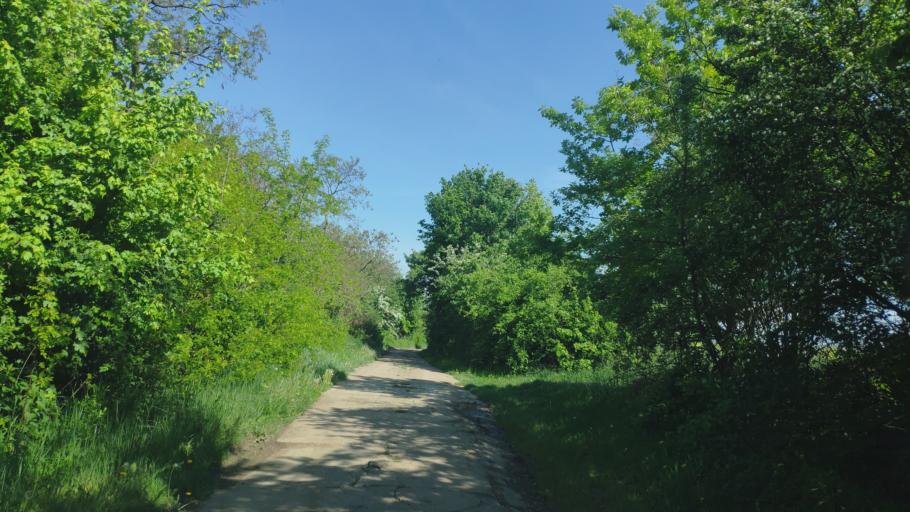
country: SK
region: Kosicky
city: Secovce
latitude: 48.6894
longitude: 21.6016
